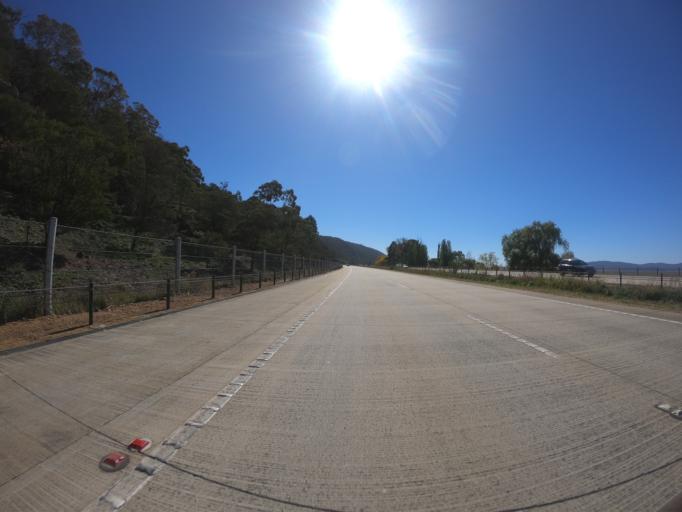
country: AU
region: New South Wales
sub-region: Yass Valley
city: Gundaroo
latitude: -35.0748
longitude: 149.3744
